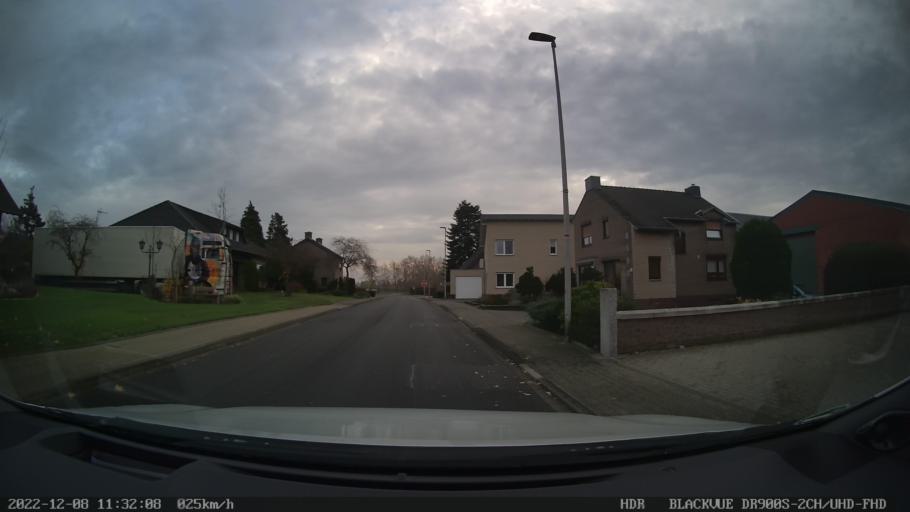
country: NL
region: Limburg
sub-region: Gemeente Sittard-Geleen
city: Sittard
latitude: 51.0397
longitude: 5.8819
